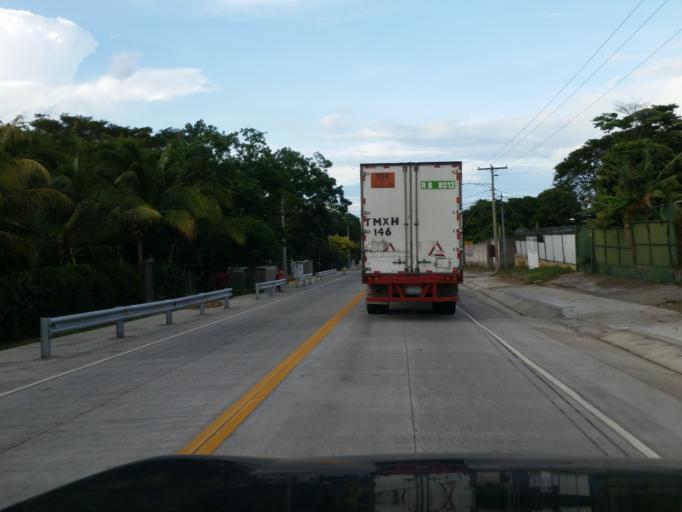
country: NI
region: Managua
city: Ciudad Sandino
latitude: 12.0869
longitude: -86.3584
